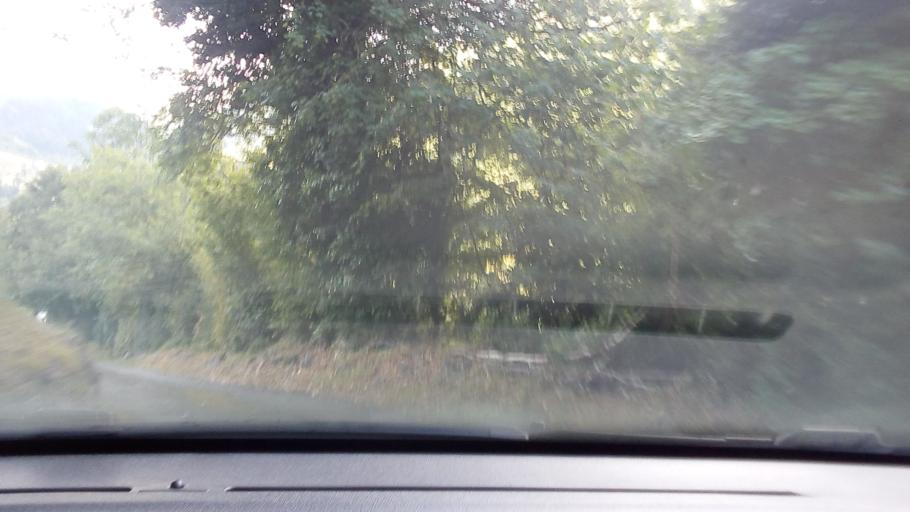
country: ES
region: Aragon
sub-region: Provincia de Huesca
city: Canfranc
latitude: 42.8544
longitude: -0.5491
